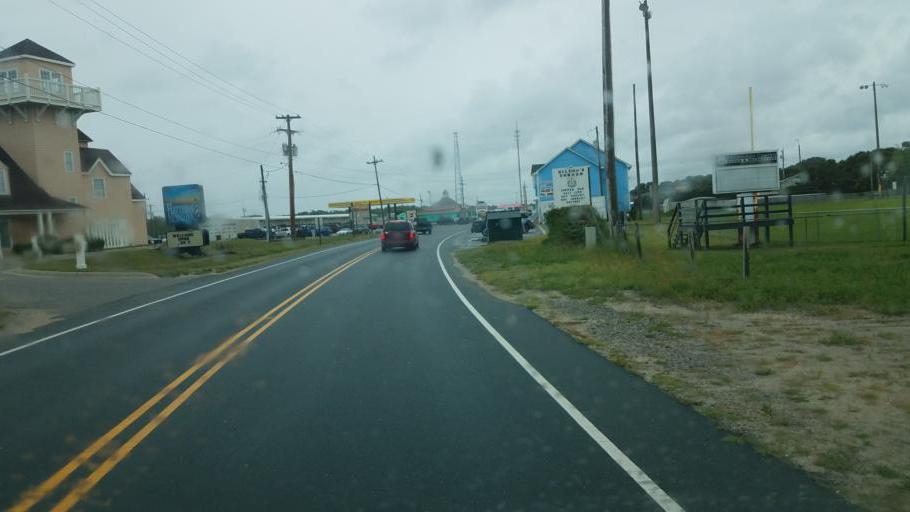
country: US
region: North Carolina
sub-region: Dare County
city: Buxton
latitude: 35.2656
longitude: -75.5207
